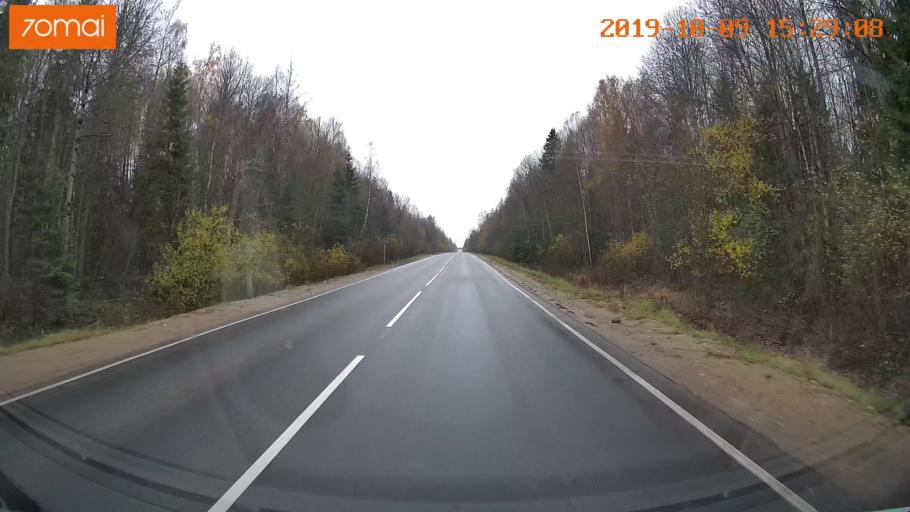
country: RU
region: Kostroma
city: Susanino
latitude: 57.9950
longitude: 41.3480
